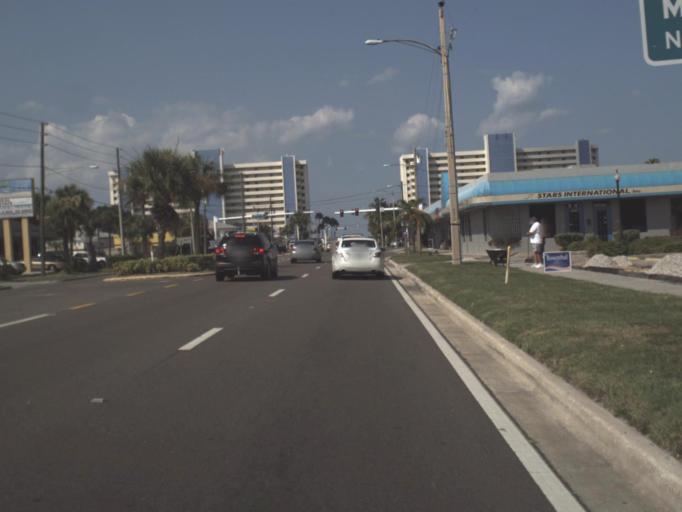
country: US
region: Florida
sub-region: Pinellas County
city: Madeira Beach
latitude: 27.8033
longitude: -82.7988
